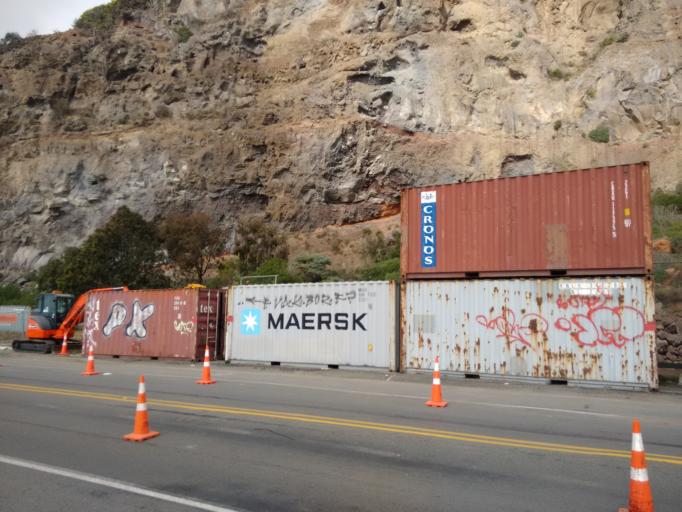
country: NZ
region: Canterbury
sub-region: Christchurch City
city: Christchurch
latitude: -43.5643
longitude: 172.7522
